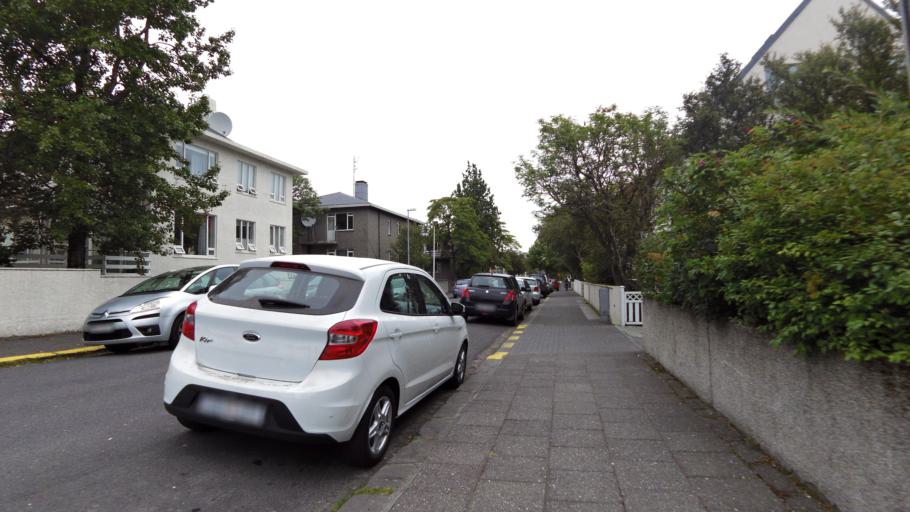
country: IS
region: Capital Region
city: Kopavogur
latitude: 64.1425
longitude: -21.9467
